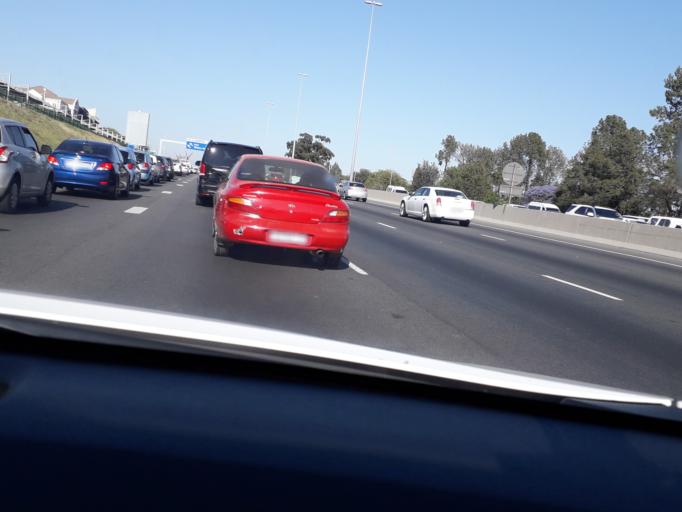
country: ZA
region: Gauteng
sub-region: City of Johannesburg Metropolitan Municipality
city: Diepsloot
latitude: -26.0371
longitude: 28.0189
